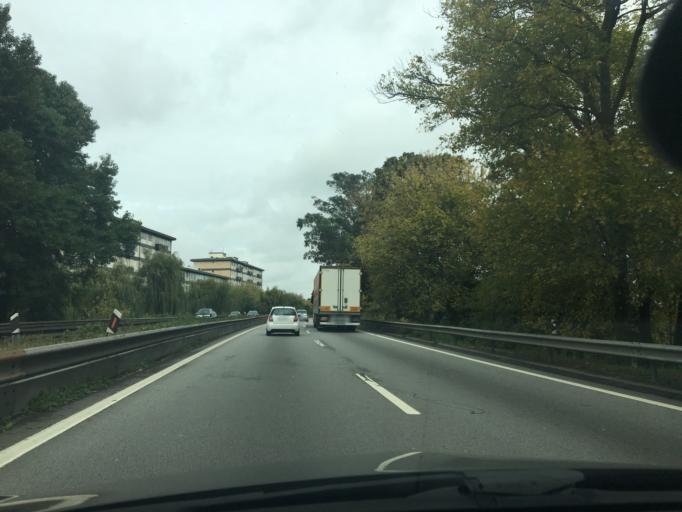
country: PT
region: Porto
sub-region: Matosinhos
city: Senhora da Hora
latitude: 41.1913
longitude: -8.6279
